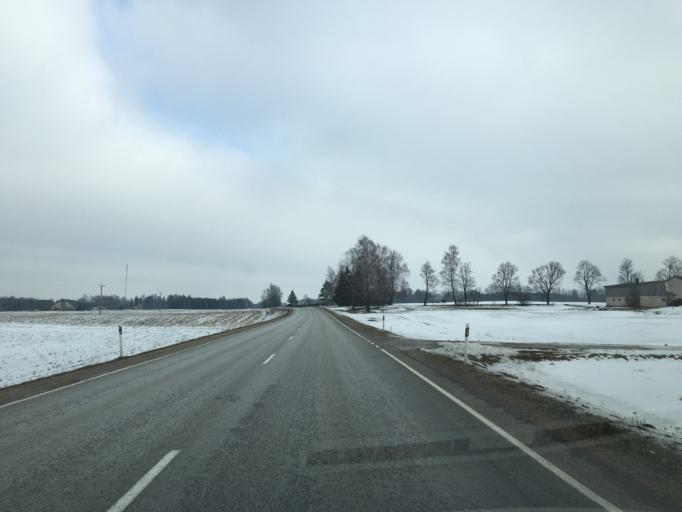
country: EE
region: Tartu
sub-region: Elva linn
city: Elva
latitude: 58.1223
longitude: 26.2423
